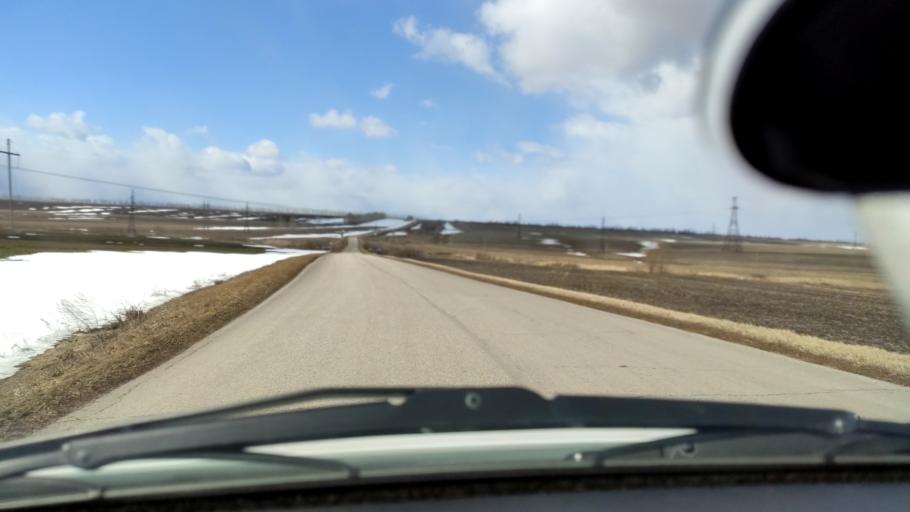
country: RU
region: Bashkortostan
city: Tolbazy
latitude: 54.1713
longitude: 55.9256
